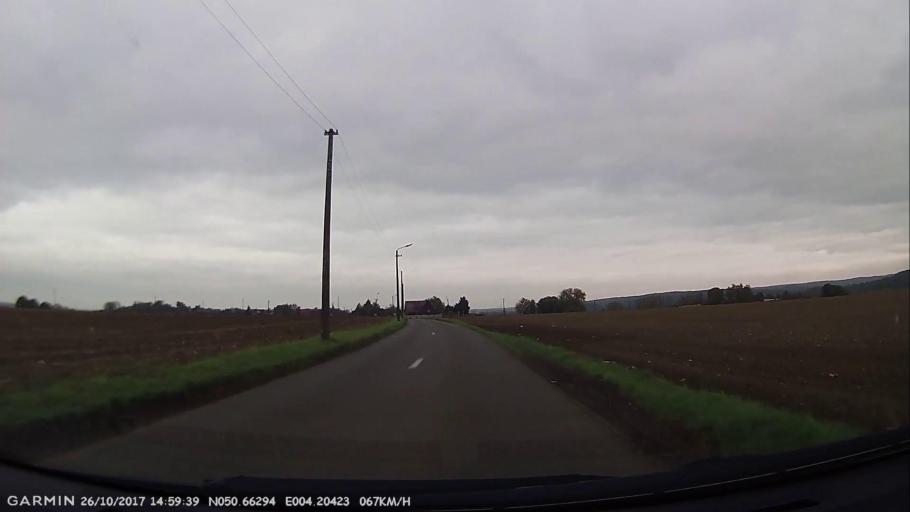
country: BE
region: Wallonia
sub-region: Province du Brabant Wallon
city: Tubize
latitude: 50.6629
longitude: 4.2042
